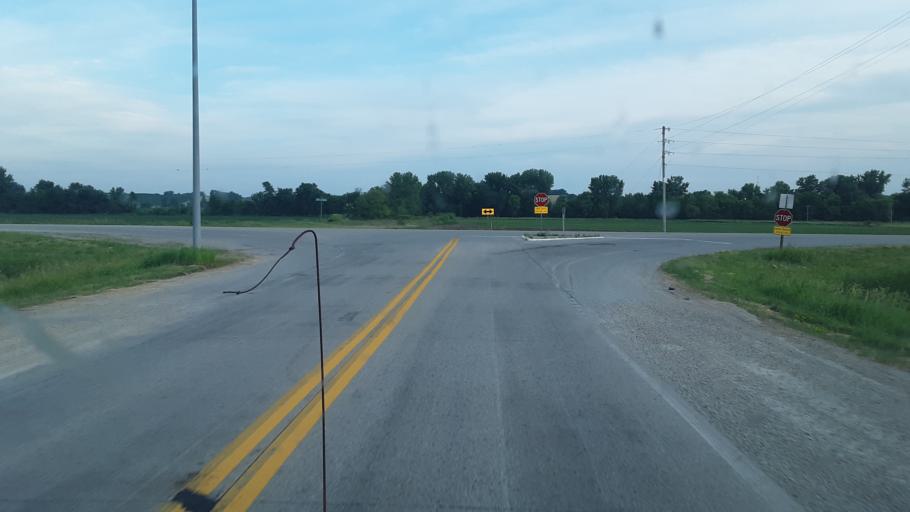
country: US
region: Iowa
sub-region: Benton County
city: Belle Plaine
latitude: 41.7432
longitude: -92.2769
